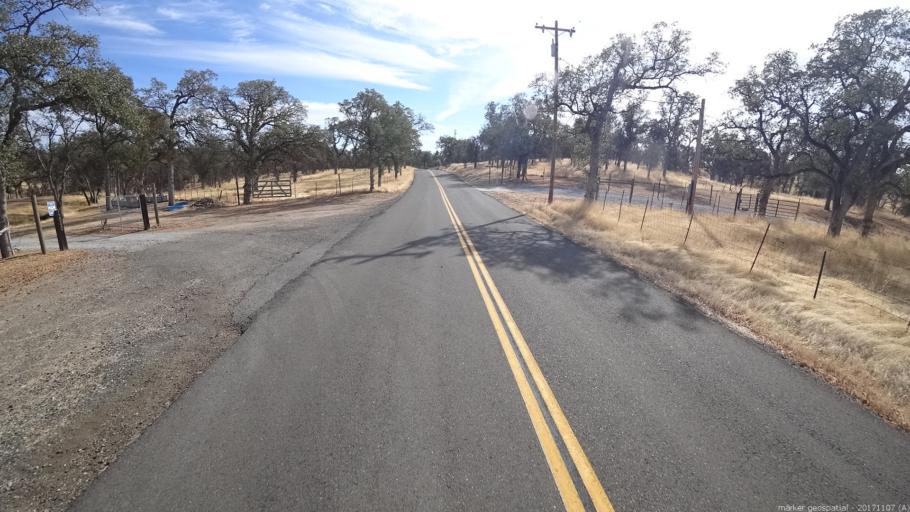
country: US
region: California
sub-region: Shasta County
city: Shasta
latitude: 40.4461
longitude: -122.5303
